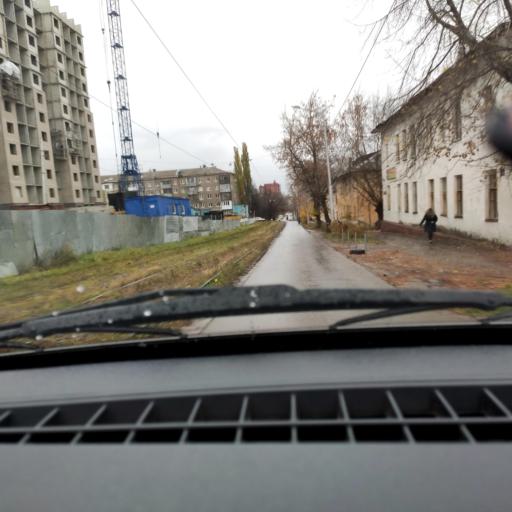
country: RU
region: Bashkortostan
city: Ufa
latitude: 54.8139
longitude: 56.0752
